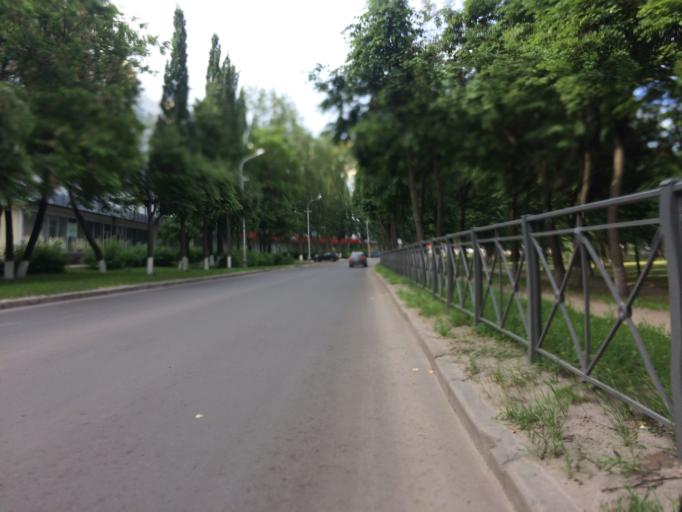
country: RU
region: Mariy-El
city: Yoshkar-Ola
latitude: 56.6268
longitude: 47.8913
